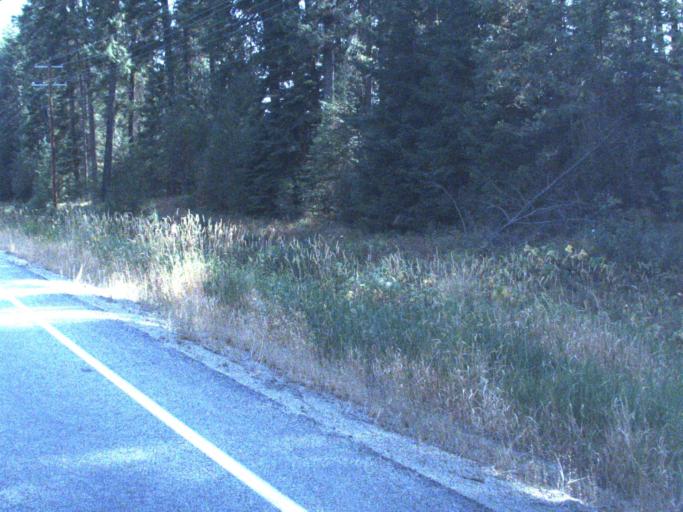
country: US
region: Washington
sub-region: Pend Oreille County
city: Newport
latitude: 48.1424
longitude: -117.2905
